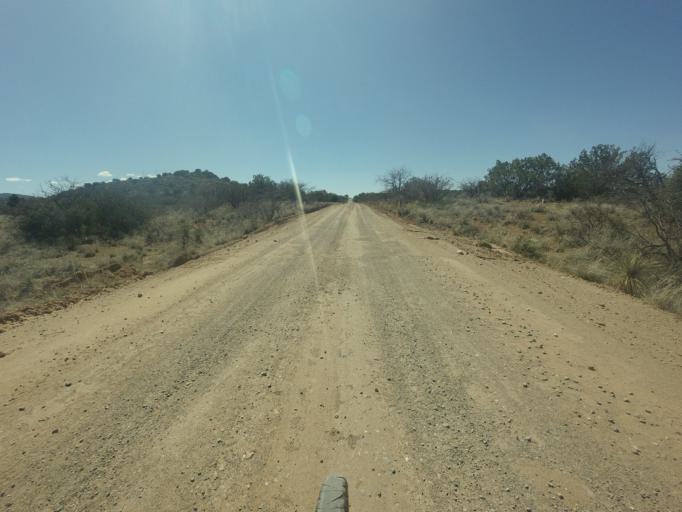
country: US
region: Arizona
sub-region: Yavapai County
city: Lake Montezuma
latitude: 34.6320
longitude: -111.7201
